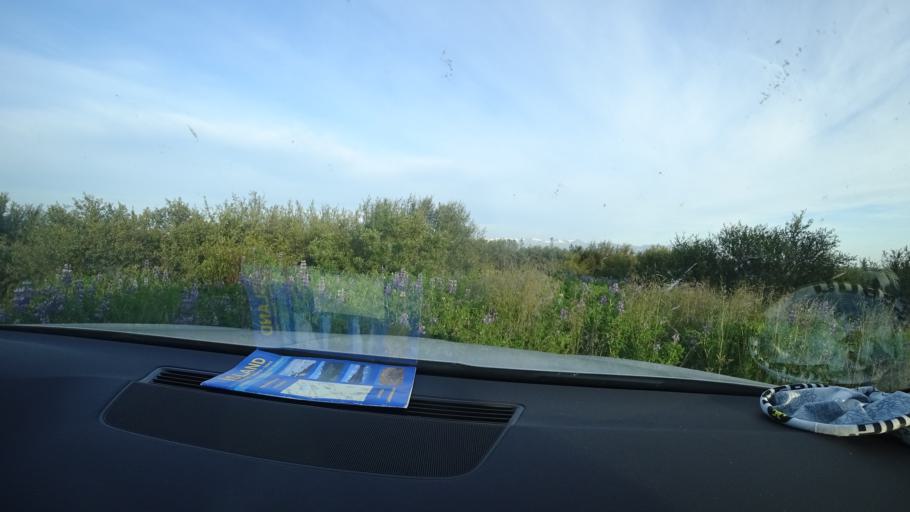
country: IS
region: West
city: Borgarnes
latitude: 64.6934
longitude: -21.9253
